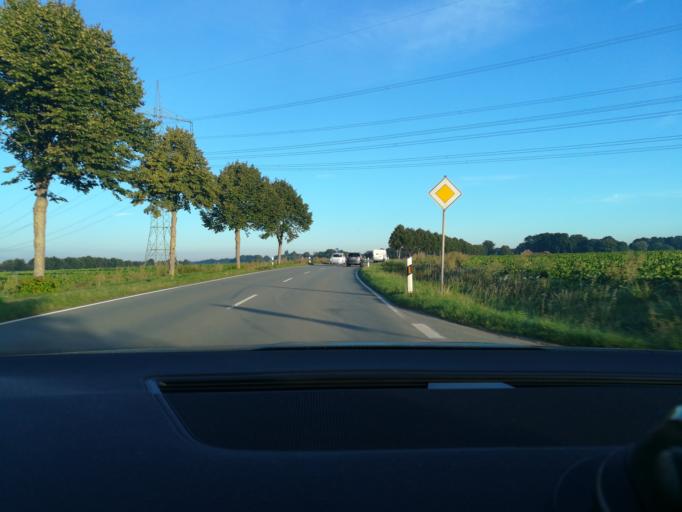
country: DE
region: North Rhine-Westphalia
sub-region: Regierungsbezirk Detmold
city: Minden
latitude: 52.3459
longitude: 8.8592
